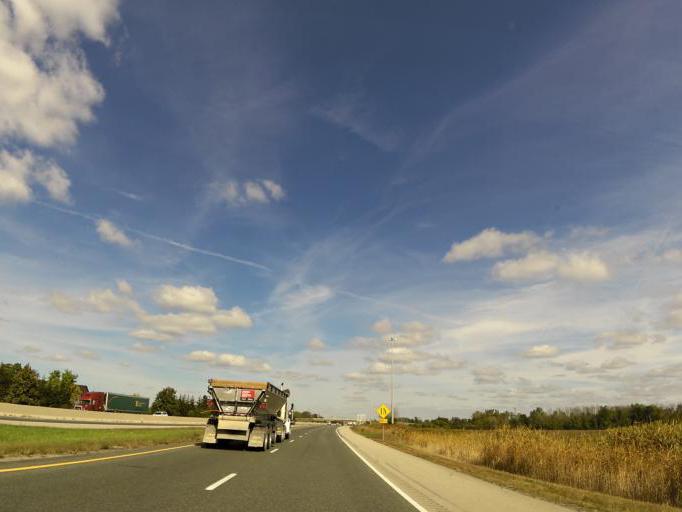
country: CA
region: Ontario
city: London
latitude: 42.9082
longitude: -81.2289
